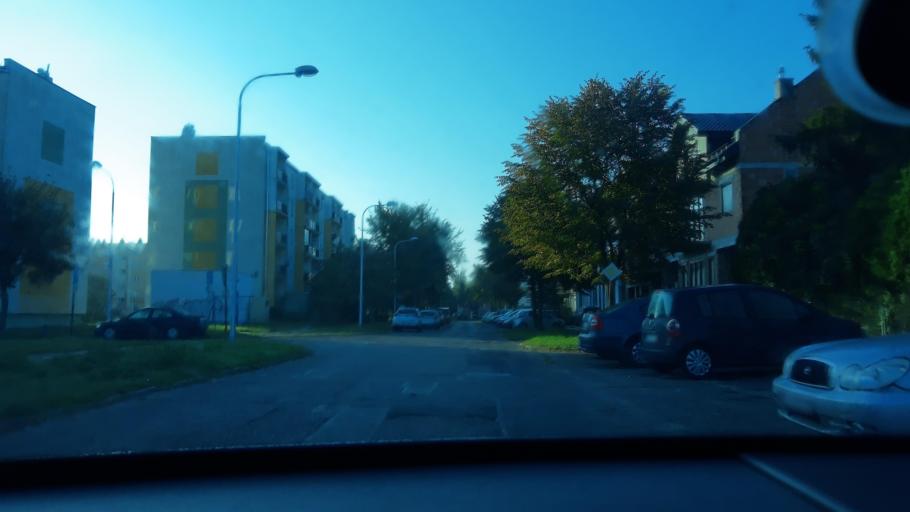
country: PL
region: Lodz Voivodeship
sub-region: Powiat sieradzki
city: Sieradz
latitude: 51.5934
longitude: 18.7103
